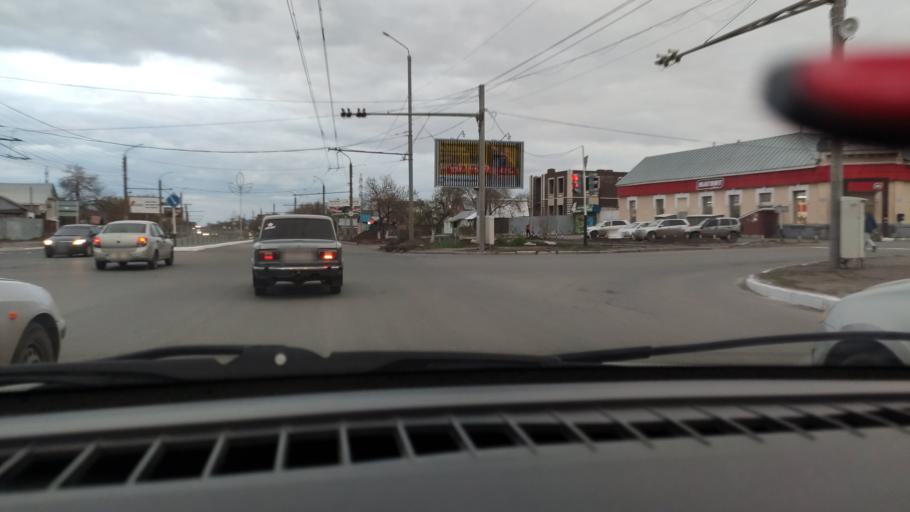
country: RU
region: Orenburg
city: Orenburg
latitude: 51.7863
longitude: 55.1066
